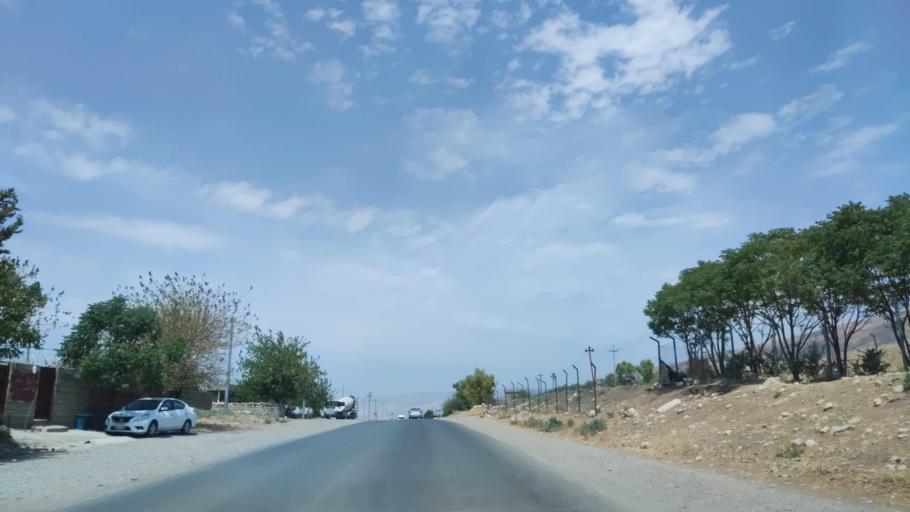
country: IQ
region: Arbil
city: Shaqlawah
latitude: 36.5281
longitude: 44.3603
